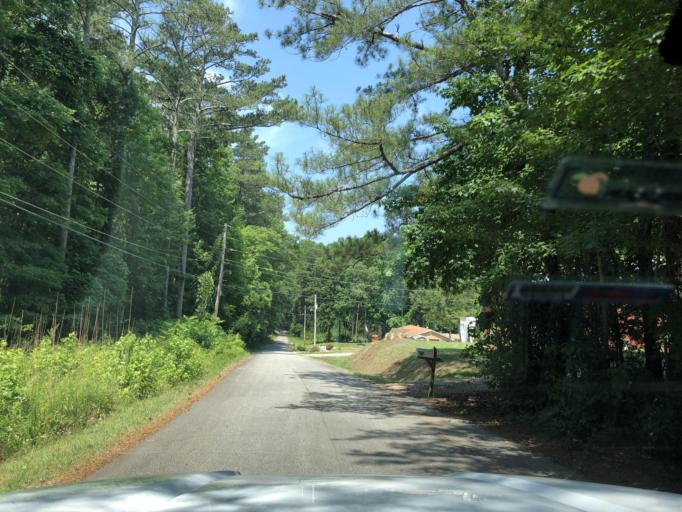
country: US
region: Georgia
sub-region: Fulton County
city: Fairburn
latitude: 33.5646
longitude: -84.5887
